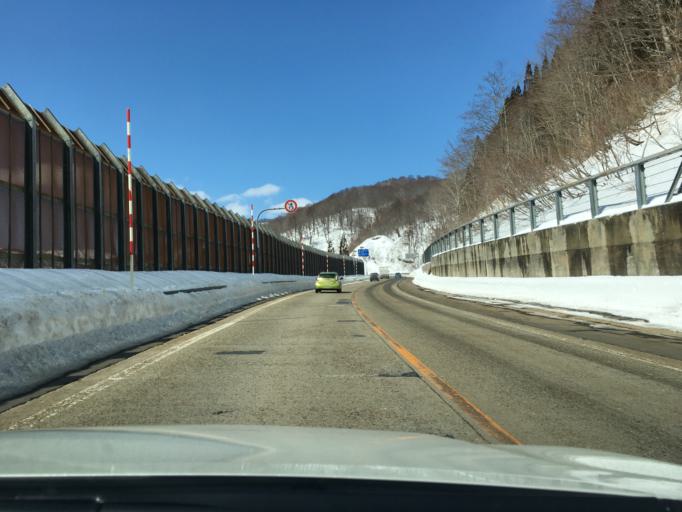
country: JP
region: Yamagata
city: Tsuruoka
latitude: 38.4845
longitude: 139.9900
